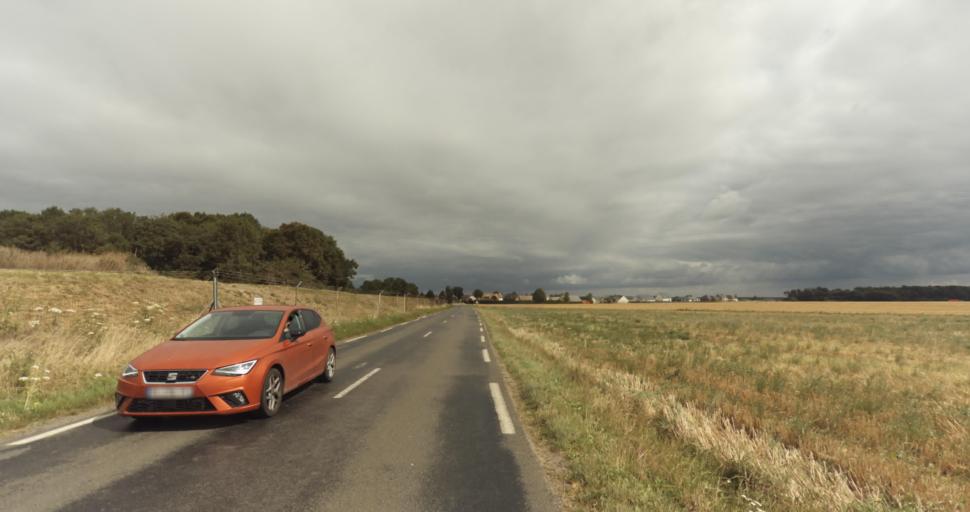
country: FR
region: Haute-Normandie
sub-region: Departement de l'Eure
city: Gravigny
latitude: 49.0271
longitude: 1.2418
